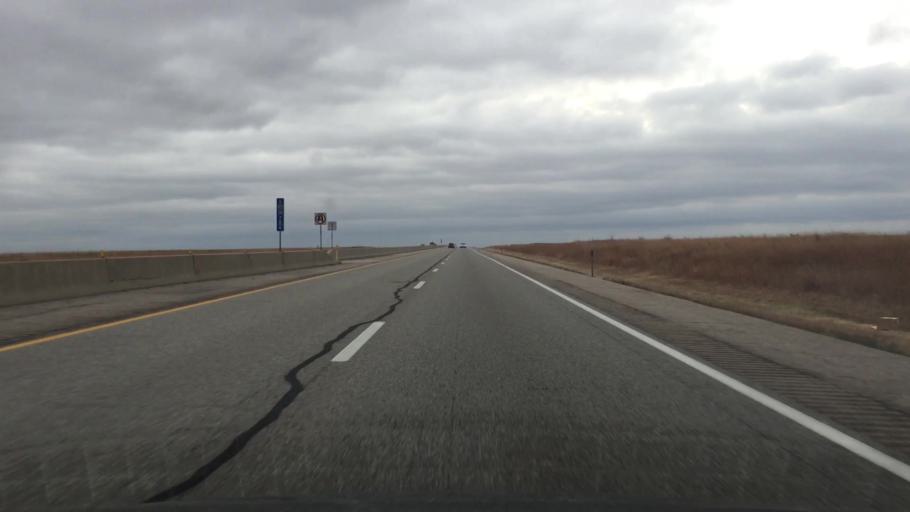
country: US
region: Kansas
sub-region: Butler County
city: El Dorado
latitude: 37.9088
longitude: -96.8153
